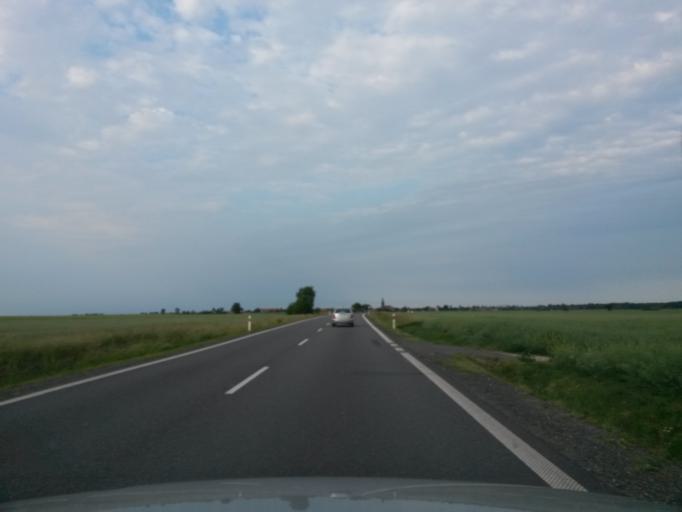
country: PL
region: Lower Silesian Voivodeship
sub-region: Powiat swidnicki
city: Zarow
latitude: 51.0037
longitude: 16.5240
